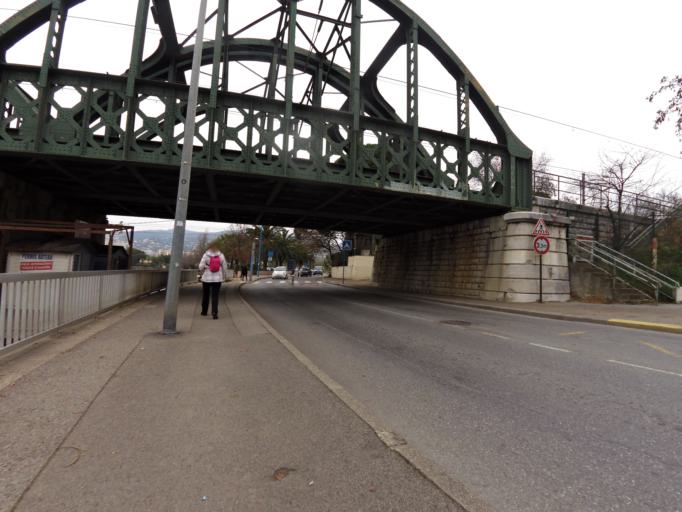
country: FR
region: Provence-Alpes-Cote d'Azur
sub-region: Departement des Alpes-Maritimes
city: Mandelieu-la-Napoule
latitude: 43.5330
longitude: 6.9466
